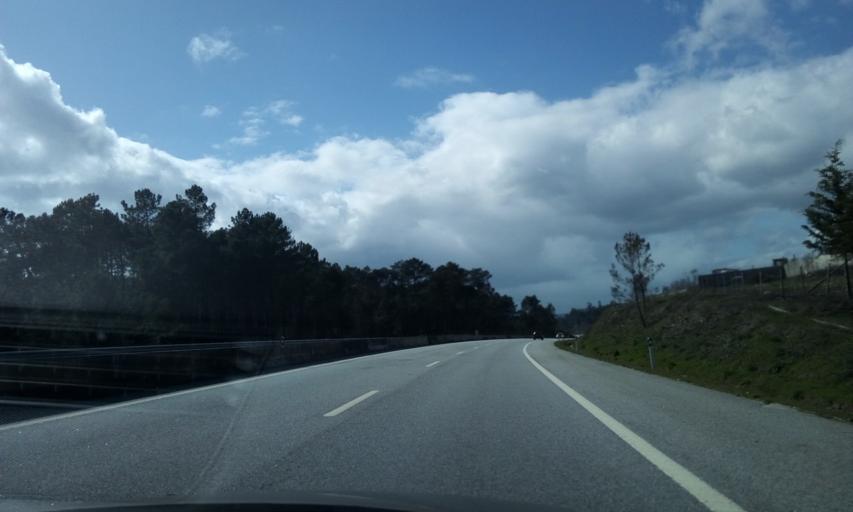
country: PT
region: Viseu
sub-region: Mangualde
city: Mangualde
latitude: 40.6203
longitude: -7.7663
